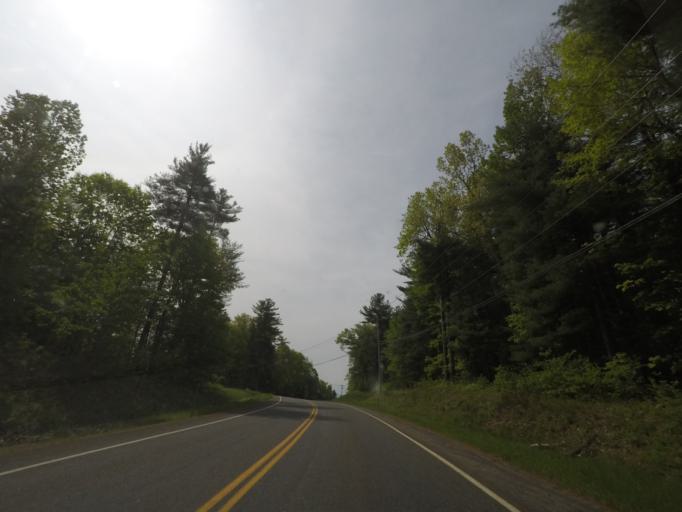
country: US
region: New York
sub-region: Saratoga County
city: Country Knolls
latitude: 42.9811
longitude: -73.7460
